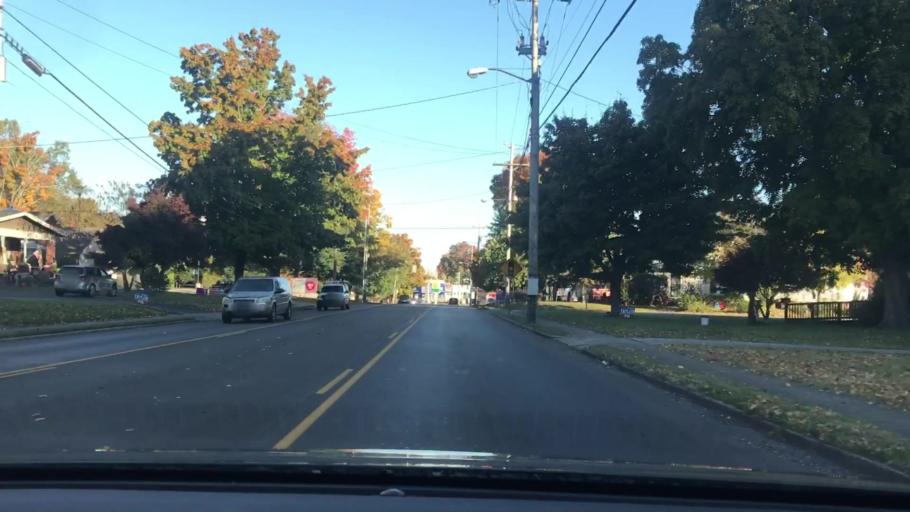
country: US
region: Kentucky
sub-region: Simpson County
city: Franklin
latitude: 36.7167
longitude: -86.5779
